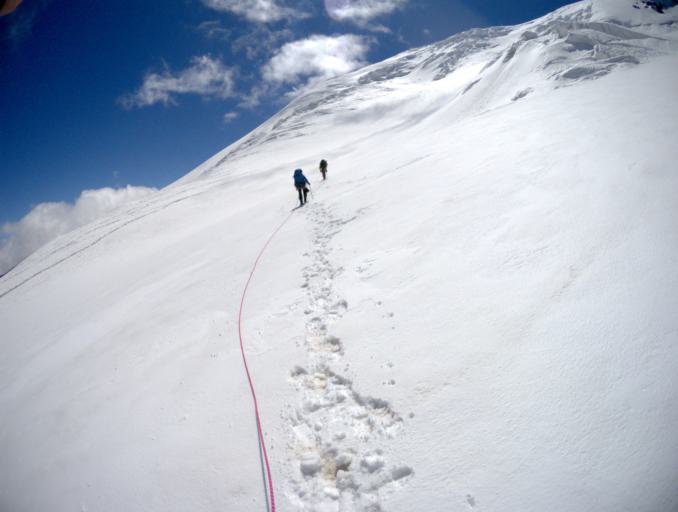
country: RU
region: Kabardino-Balkariya
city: Terskol
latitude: 43.3807
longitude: 42.4479
